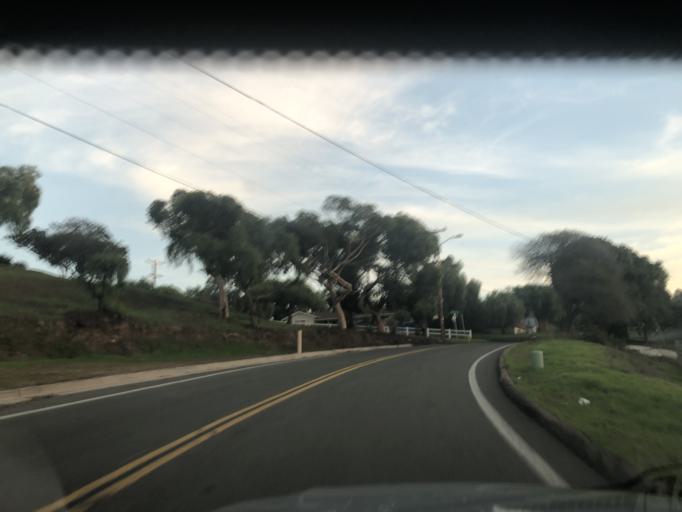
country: US
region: California
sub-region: San Diego County
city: Chula Vista
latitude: 32.6459
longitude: -117.0618
